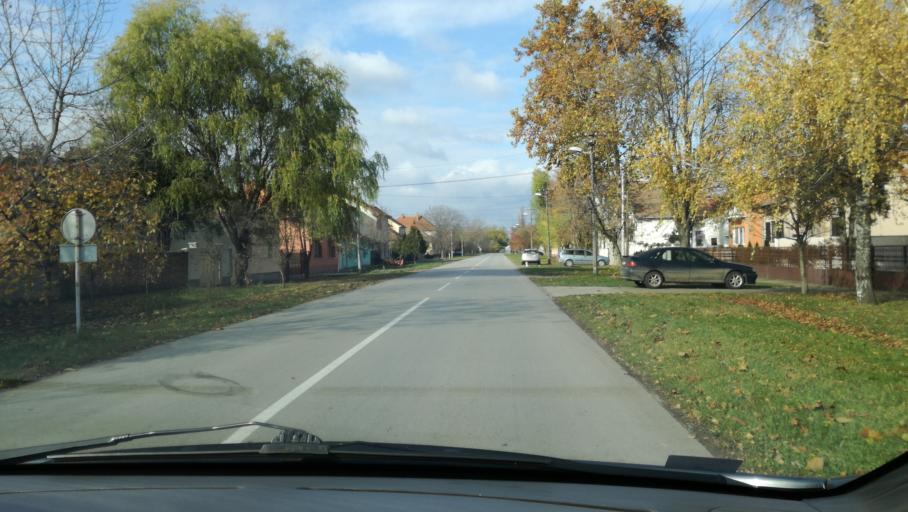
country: RS
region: Autonomna Pokrajina Vojvodina
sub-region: Severnobanatski Okrug
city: Kikinda
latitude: 45.8359
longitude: 20.4566
